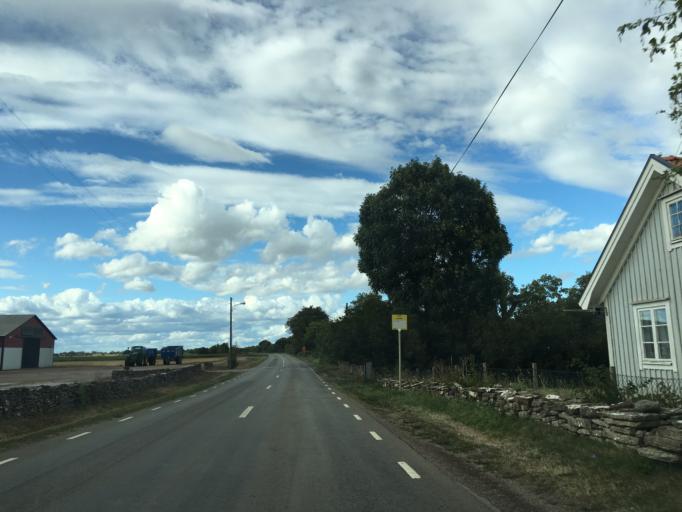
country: SE
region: Kalmar
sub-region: Morbylanga Kommun
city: Moerbylanga
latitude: 56.4206
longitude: 16.4355
